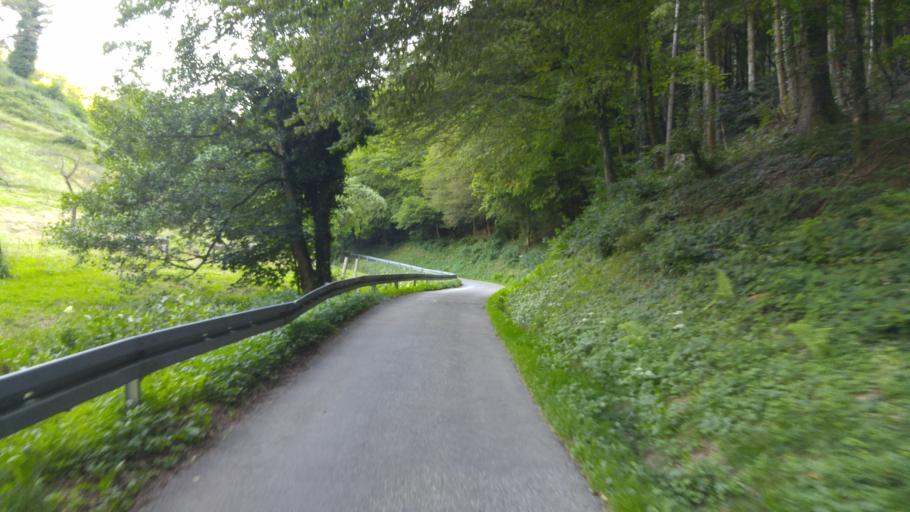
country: DE
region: Baden-Wuerttemberg
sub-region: Freiburg Region
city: Muenstertal/Schwarzwald
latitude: 47.8378
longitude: 7.7894
